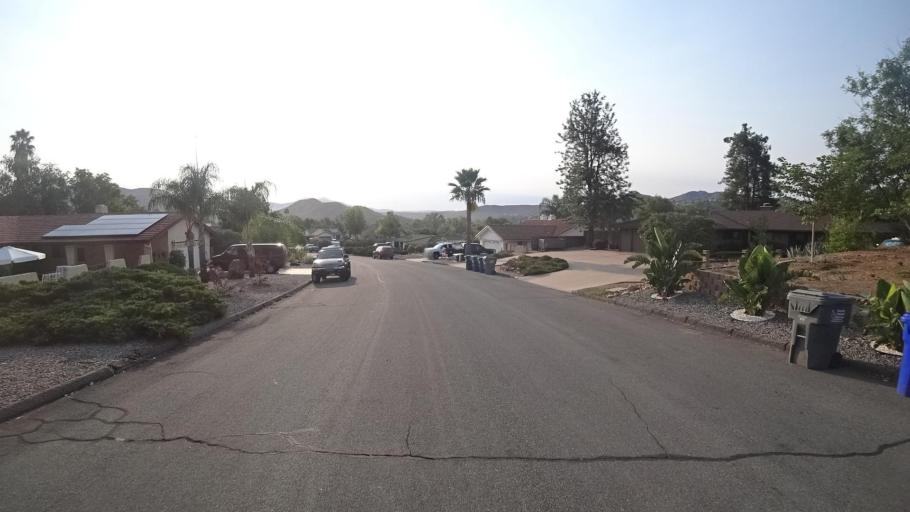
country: US
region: California
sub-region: San Diego County
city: San Diego Country Estates
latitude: 33.0120
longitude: -116.8242
